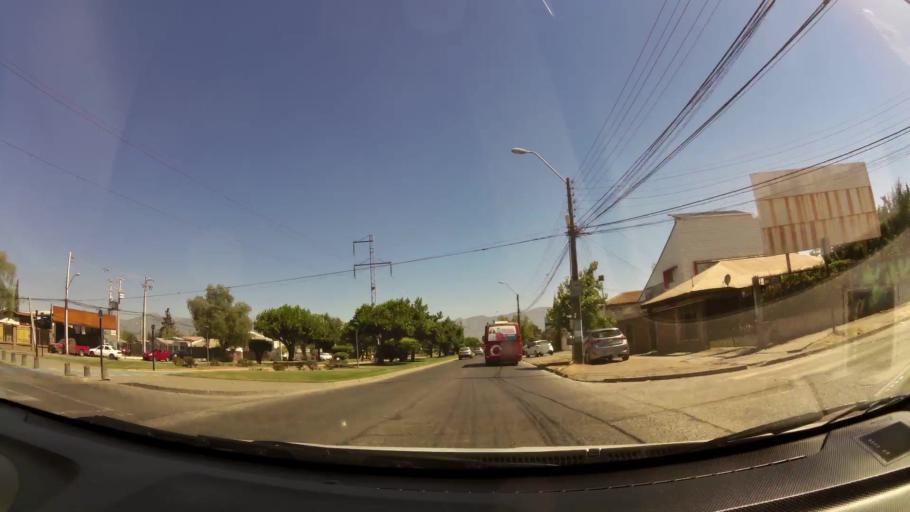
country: CL
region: O'Higgins
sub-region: Provincia de Cachapoal
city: Rancagua
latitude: -34.1702
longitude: -70.7162
